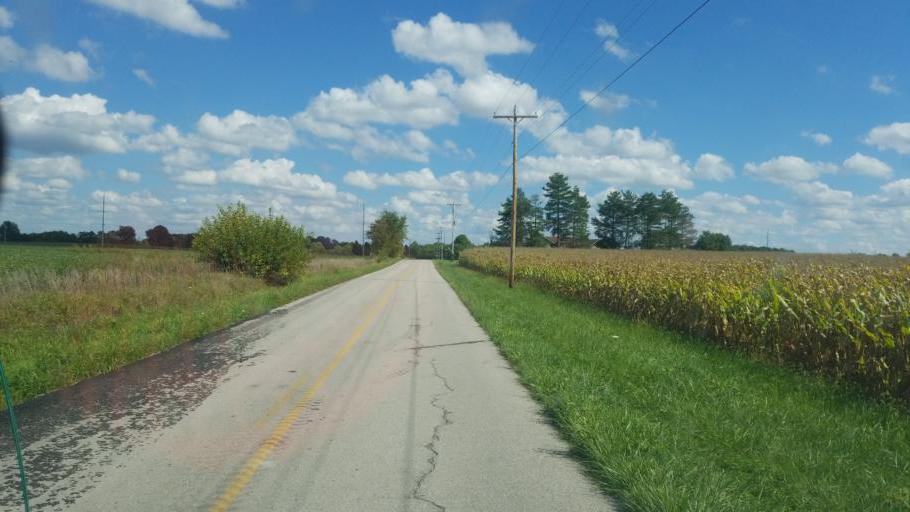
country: US
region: Ohio
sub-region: Delaware County
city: Delaware
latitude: 40.3106
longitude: -83.2033
